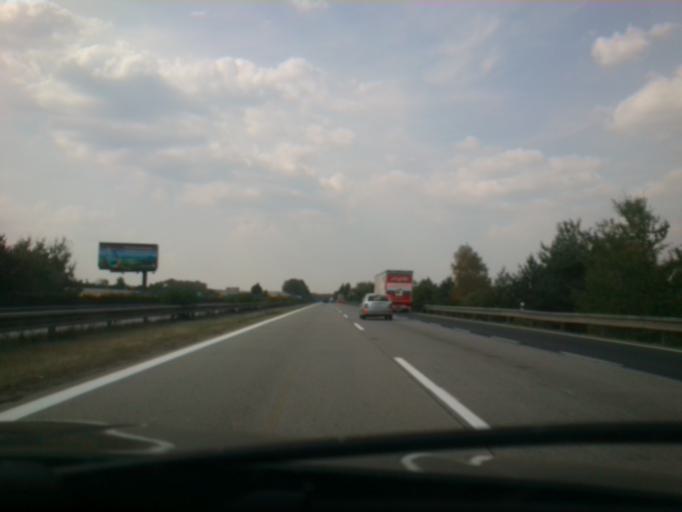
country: CZ
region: Central Bohemia
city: Divisov
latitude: 49.8188
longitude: 14.8748
